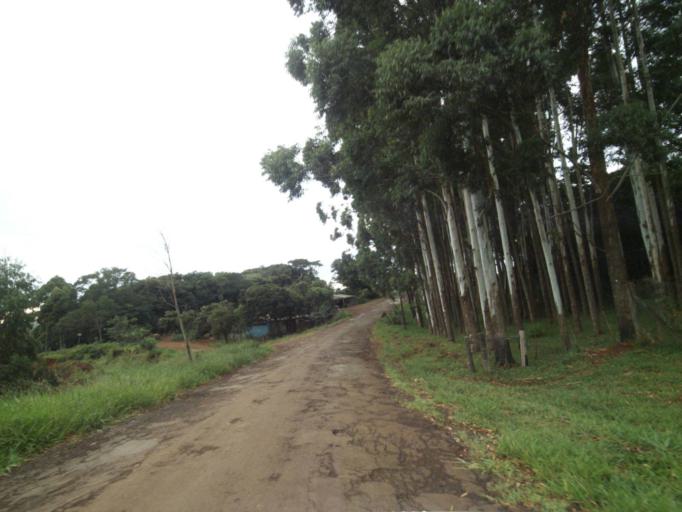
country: BR
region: Parana
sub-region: Guaraniacu
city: Guaraniacu
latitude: -25.1189
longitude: -52.8502
